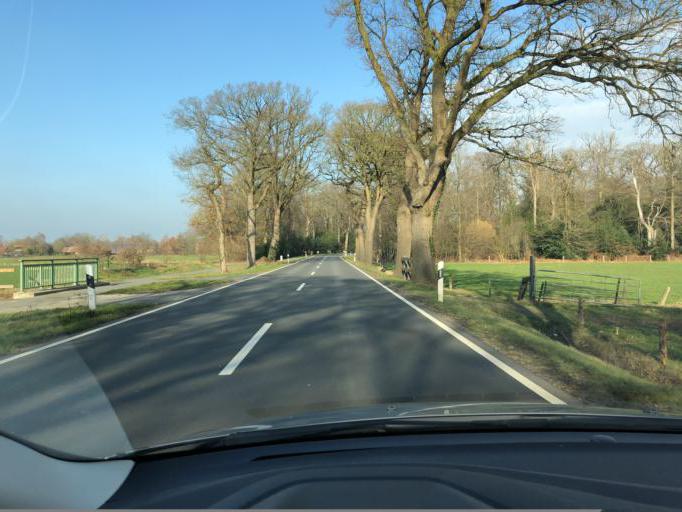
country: DE
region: Lower Saxony
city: Westerstede
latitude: 53.2675
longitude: 7.9083
